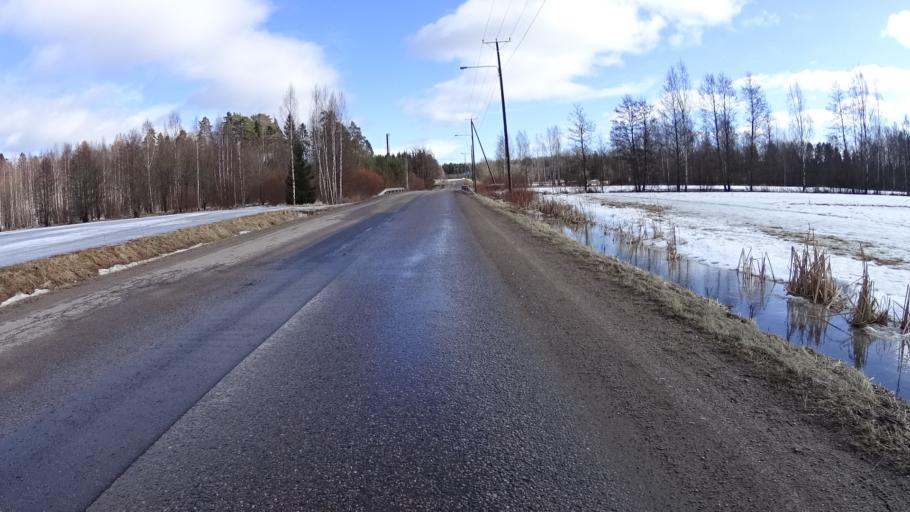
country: FI
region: Uusimaa
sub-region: Helsinki
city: Espoo
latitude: 60.2745
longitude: 24.6622
